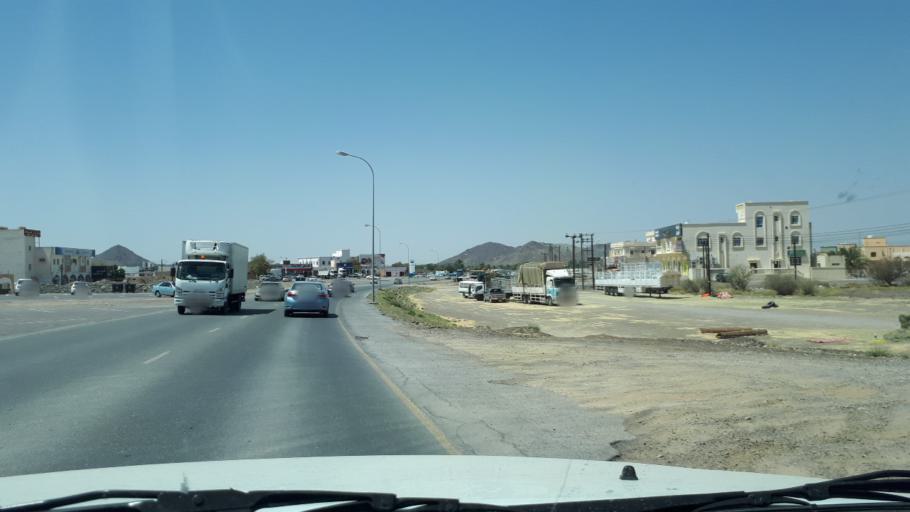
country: OM
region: Muhafazat ad Dakhiliyah
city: Bahla'
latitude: 22.9506
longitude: 57.2862
